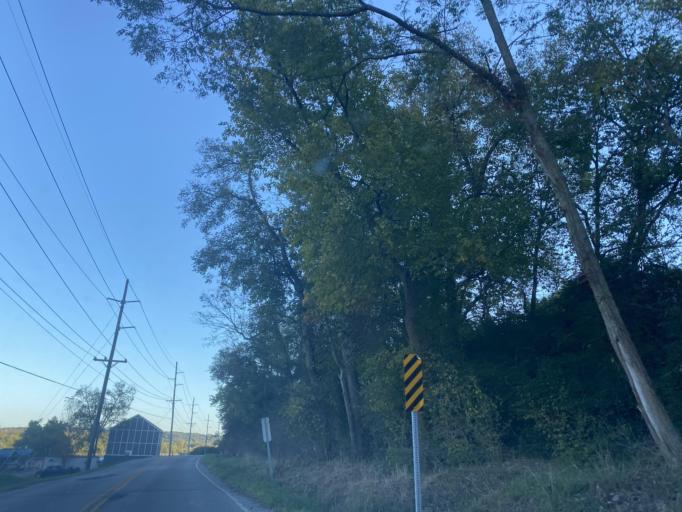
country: US
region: Kentucky
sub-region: Campbell County
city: Dayton
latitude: 39.1106
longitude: -84.4501
